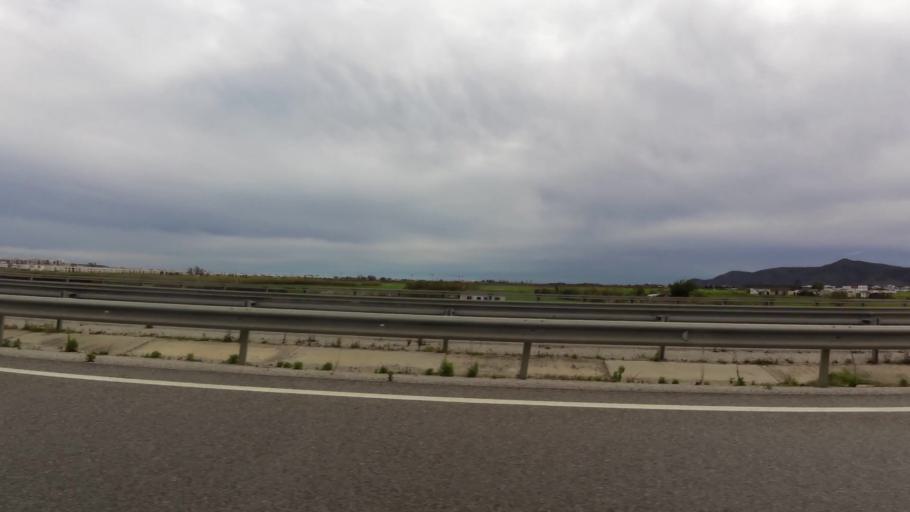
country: MA
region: Tanger-Tetouan
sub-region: Tetouan
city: Martil
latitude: 35.7082
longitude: -5.3558
